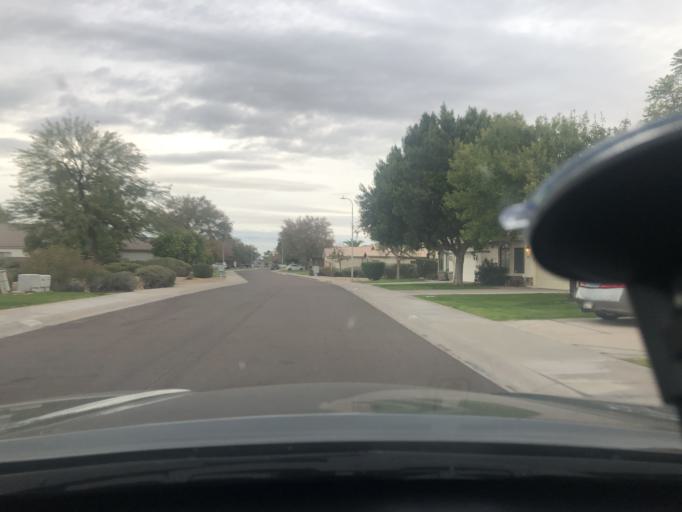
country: US
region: Arizona
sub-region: Maricopa County
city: Scottsdale
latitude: 33.4810
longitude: -111.9020
